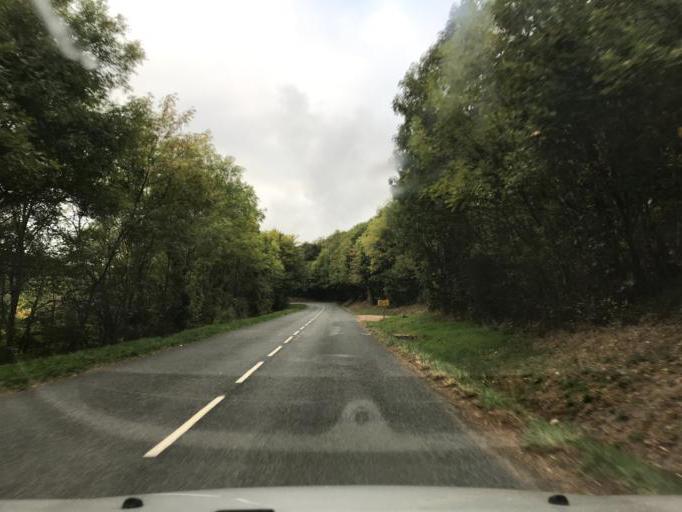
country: FR
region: Rhone-Alpes
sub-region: Departement du Rhone
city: Cogny
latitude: 46.0145
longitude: 4.5790
